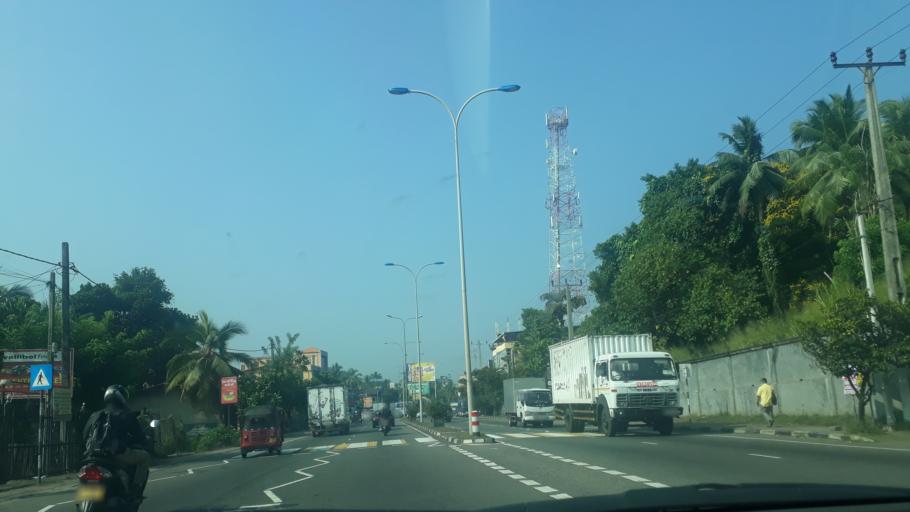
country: LK
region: Western
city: Kelaniya
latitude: 6.9965
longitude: 79.9477
